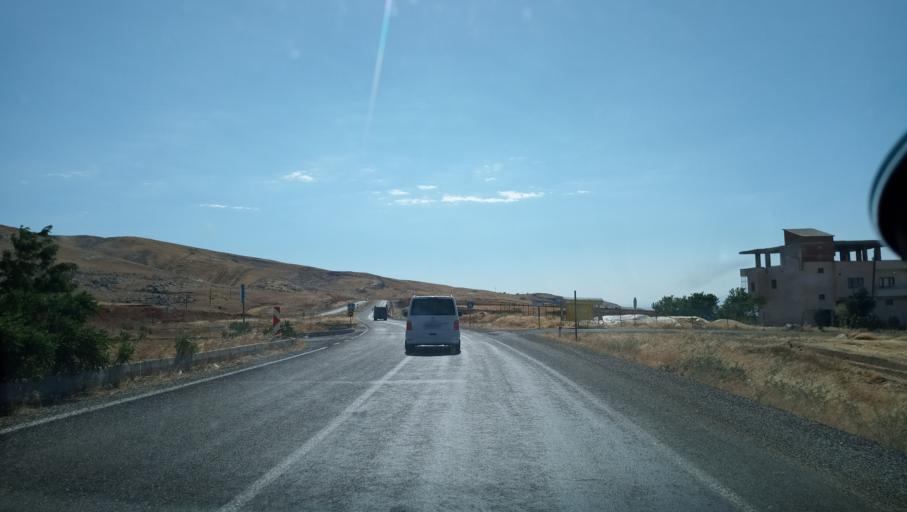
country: TR
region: Diyarbakir
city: Silvan
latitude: 38.1278
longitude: 41.0781
